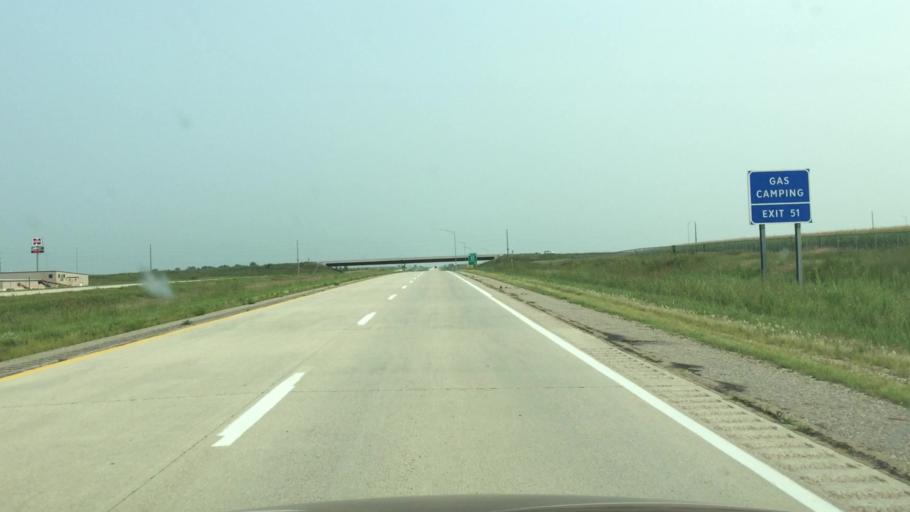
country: US
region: Iowa
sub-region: Osceola County
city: Sibley
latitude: 43.4000
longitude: -95.7171
